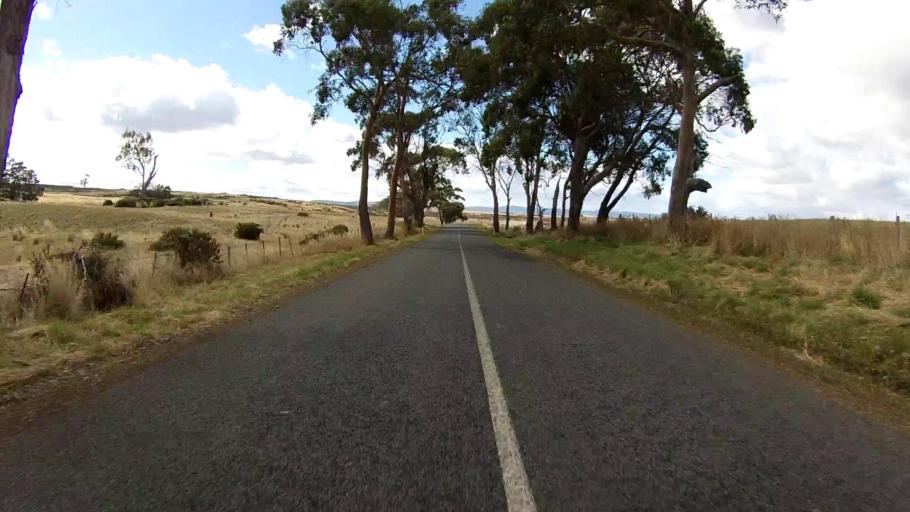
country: AU
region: Tasmania
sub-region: Northern Midlands
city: Evandale
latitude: -41.7031
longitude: 147.3845
